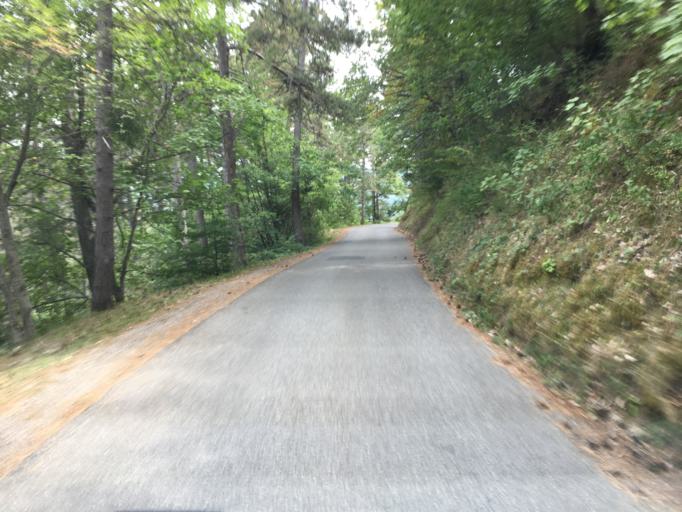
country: FR
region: Provence-Alpes-Cote d'Azur
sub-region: Departement des Alpes-de-Haute-Provence
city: Digne-les-Bains
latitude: 44.2076
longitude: 6.1507
